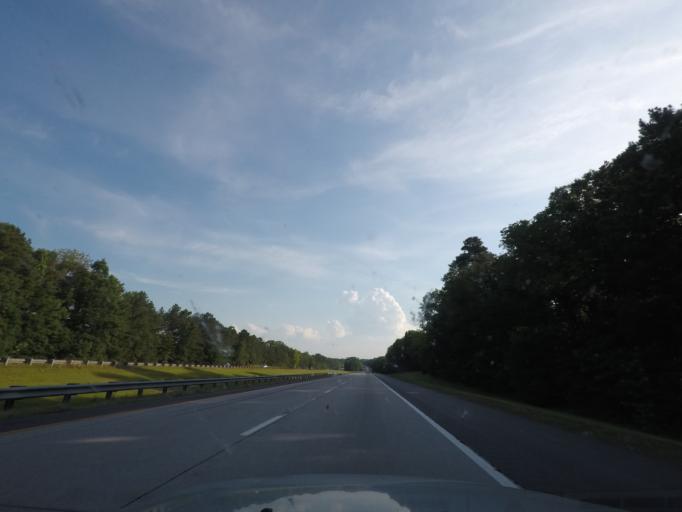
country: US
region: North Carolina
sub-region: Granville County
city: Creedmoor
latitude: 36.1897
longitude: -78.6879
